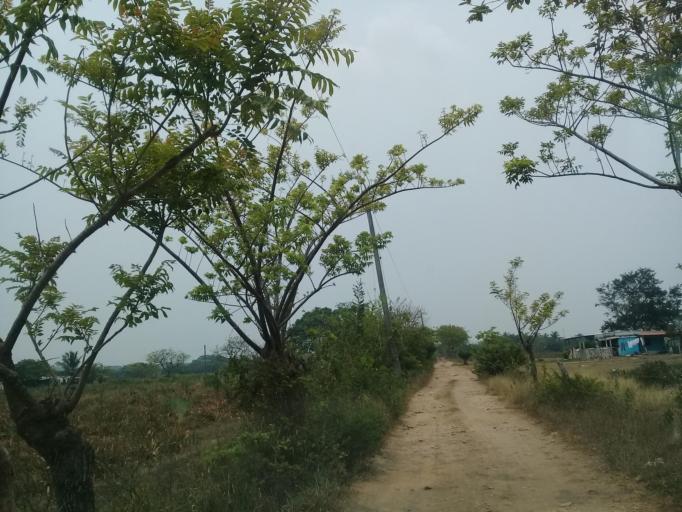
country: MX
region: Veracruz
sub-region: Medellin
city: La Laguna y Monte del Castillo
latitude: 18.9727
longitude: -96.1376
